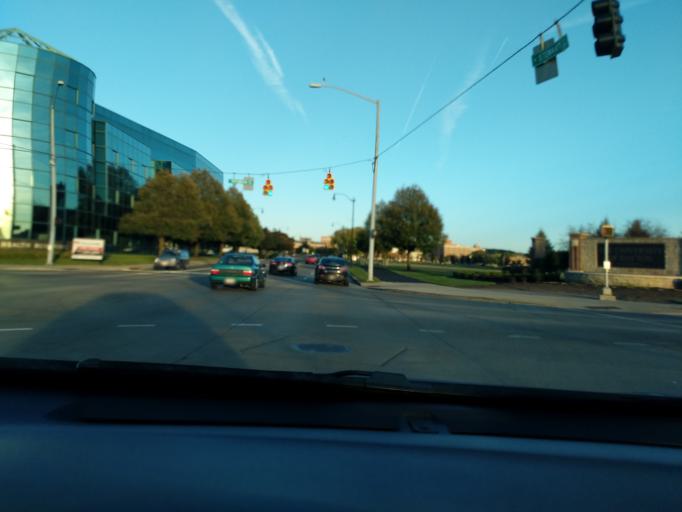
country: US
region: Ohio
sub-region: Montgomery County
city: Dayton
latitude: 39.7400
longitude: -84.1921
